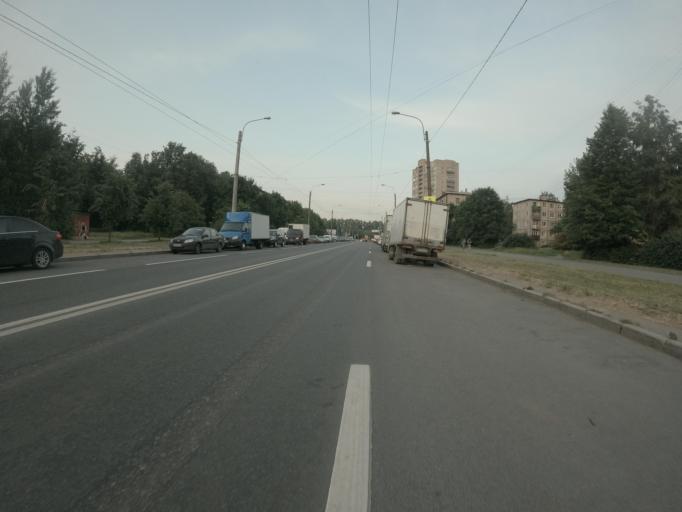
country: RU
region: Leningrad
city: Kalininskiy
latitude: 59.9690
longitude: 30.4063
